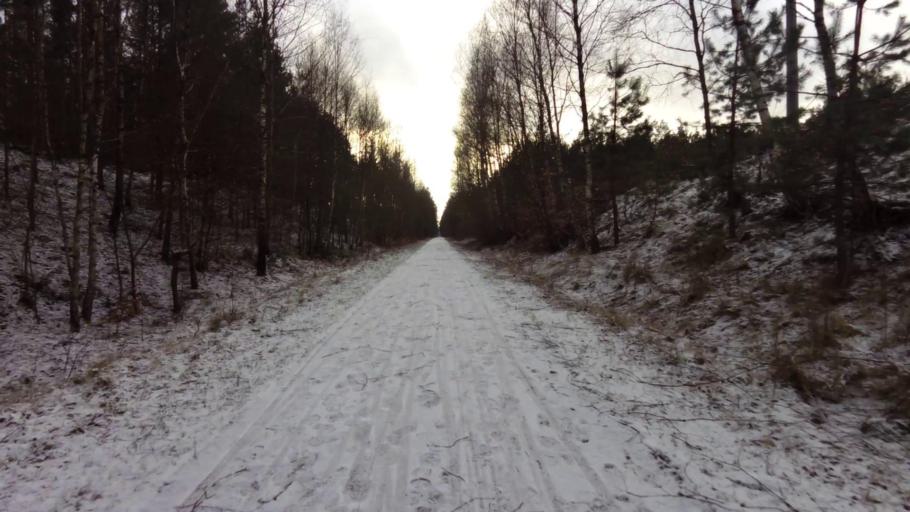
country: PL
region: West Pomeranian Voivodeship
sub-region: Powiat drawski
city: Zlocieniec
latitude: 53.5609
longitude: 16.0324
